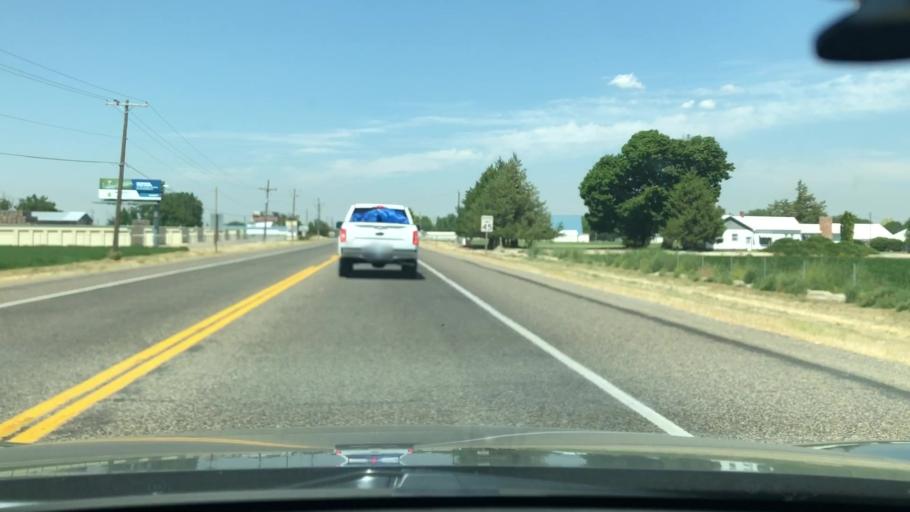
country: US
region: Idaho
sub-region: Canyon County
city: Wilder
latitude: 43.6654
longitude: -116.9118
